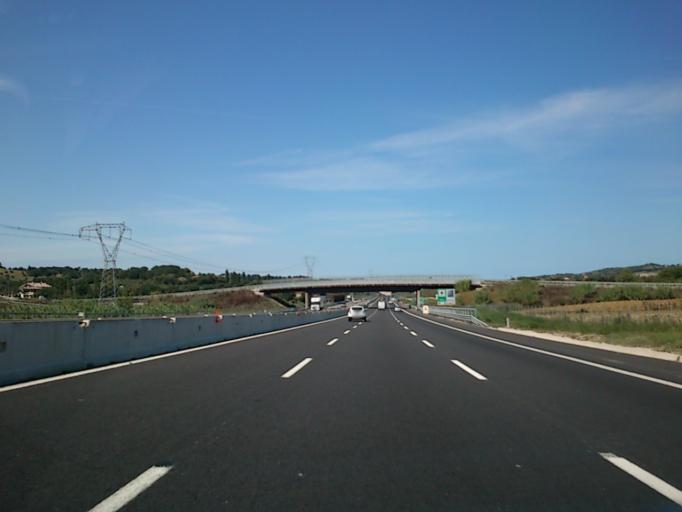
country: IT
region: The Marches
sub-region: Provincia di Pesaro e Urbino
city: Villa Ceccolini
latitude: 43.9021
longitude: 12.8302
